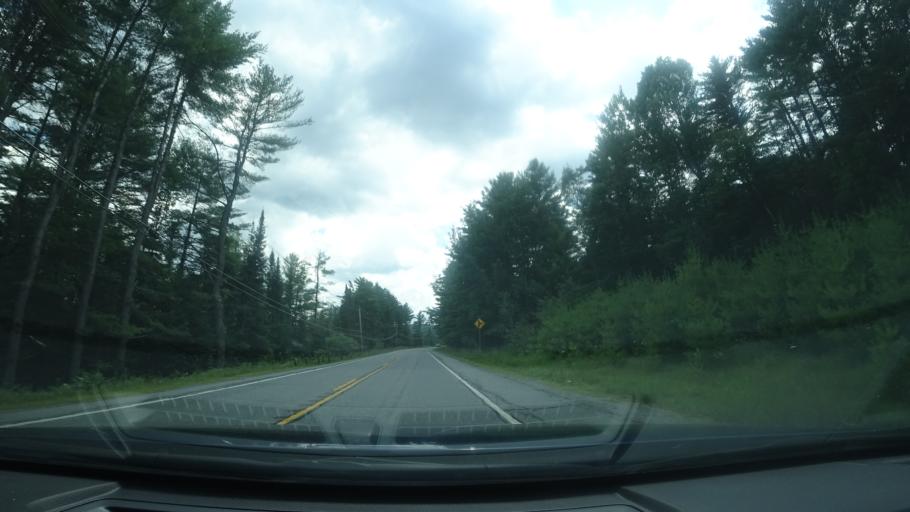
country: US
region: New York
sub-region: Warren County
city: Warrensburg
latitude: 43.5260
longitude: -73.7895
